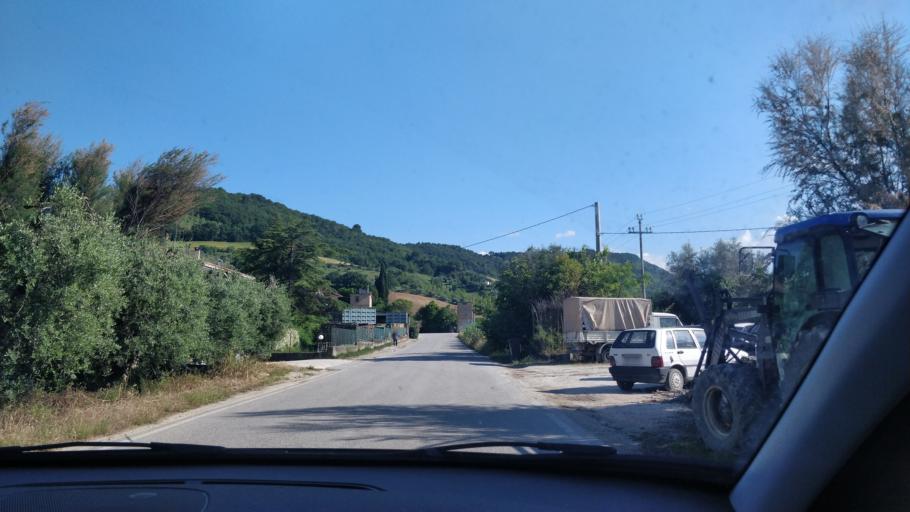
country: IT
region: The Marches
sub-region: Provincia di Ascoli Piceno
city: Massignano
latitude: 43.0353
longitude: 13.8003
